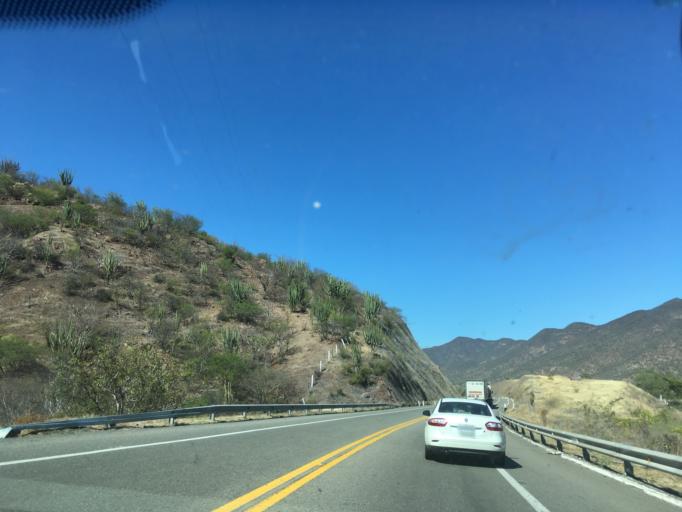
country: MX
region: Michoacan
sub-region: Arteaga
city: Las Canas
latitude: 18.4421
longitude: -101.9277
